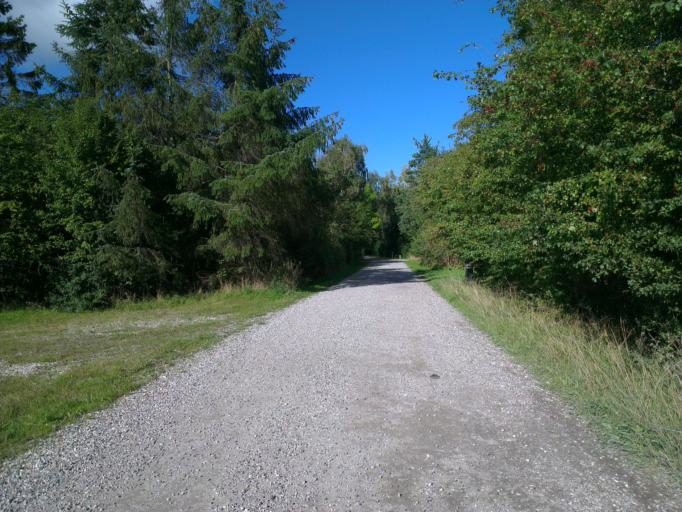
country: DK
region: Capital Region
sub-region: Frederikssund Kommune
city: Frederikssund
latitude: 55.7922
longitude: 12.0489
